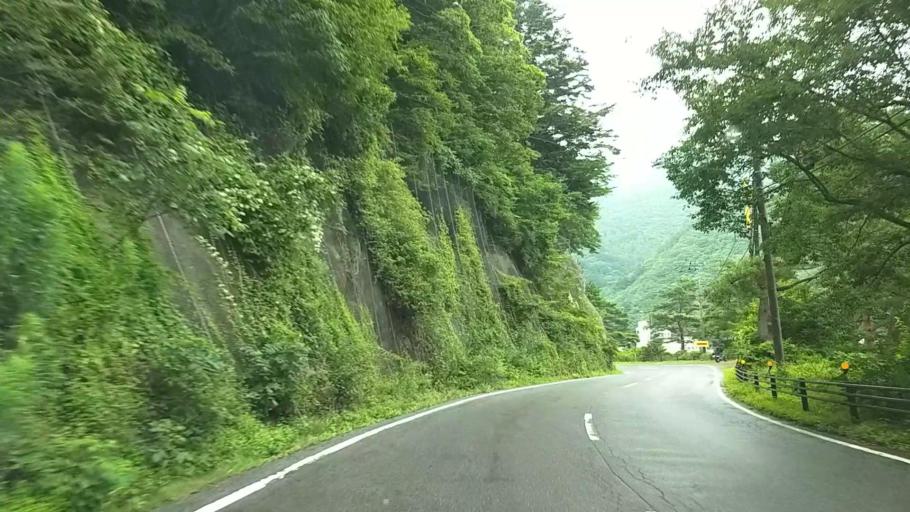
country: JP
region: Yamanashi
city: Fujikawaguchiko
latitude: 35.4884
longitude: 138.6041
